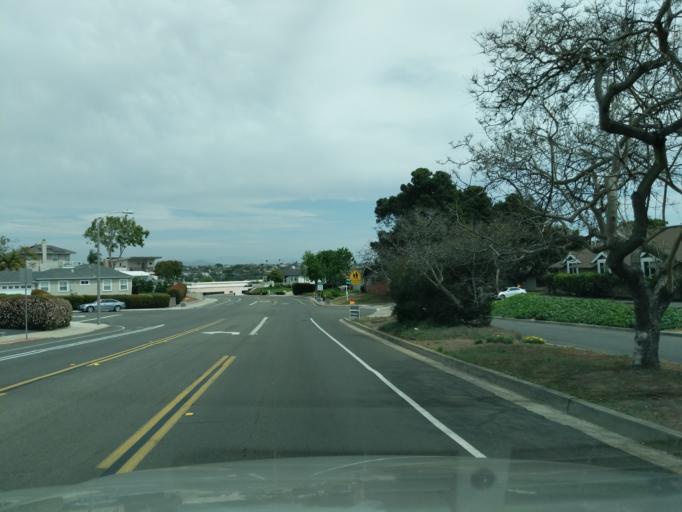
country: US
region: California
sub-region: San Diego County
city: Coronado
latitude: 32.7325
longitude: -117.2358
